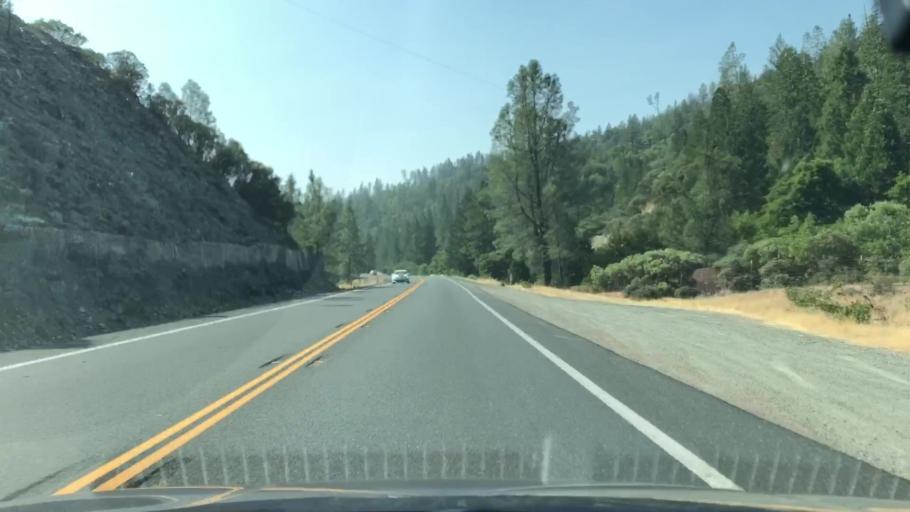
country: US
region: California
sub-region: Lake County
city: Middletown
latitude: 38.6925
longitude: -122.5978
